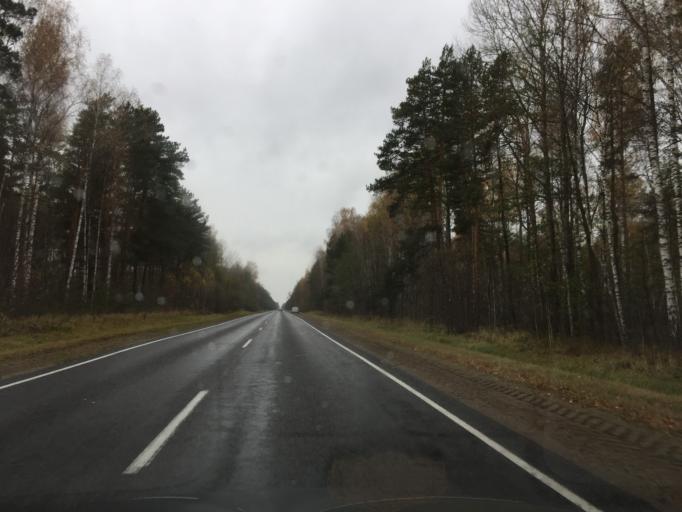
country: BY
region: Mogilev
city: Slawharad
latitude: 53.3591
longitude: 30.8392
